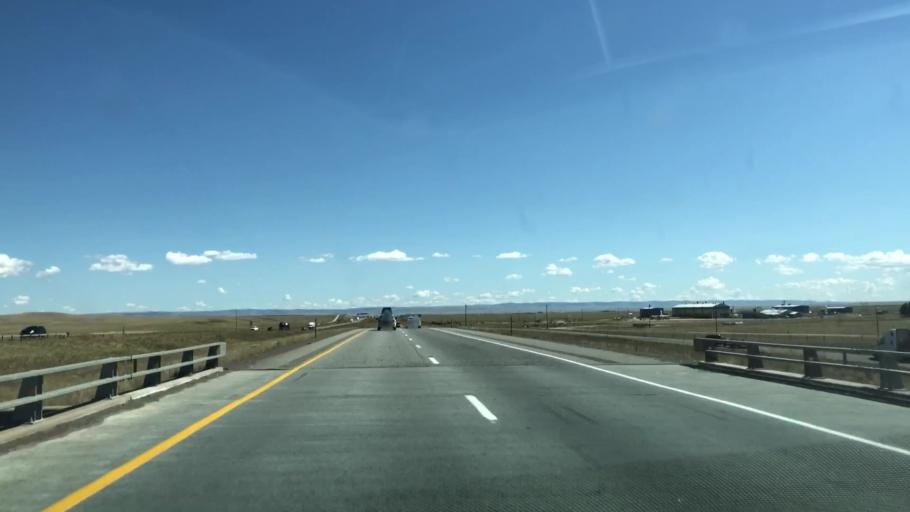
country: US
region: Wyoming
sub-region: Albany County
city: Laramie
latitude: 41.4404
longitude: -105.9436
